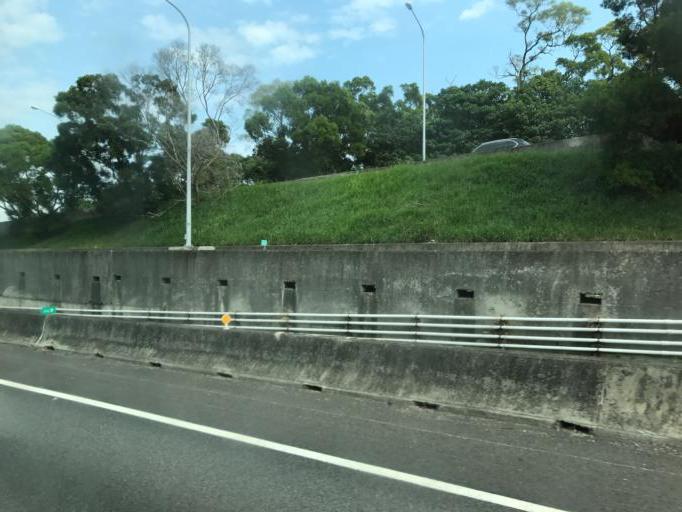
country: TW
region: Taiwan
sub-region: Hsinchu
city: Zhubei
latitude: 24.7989
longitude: 121.0088
